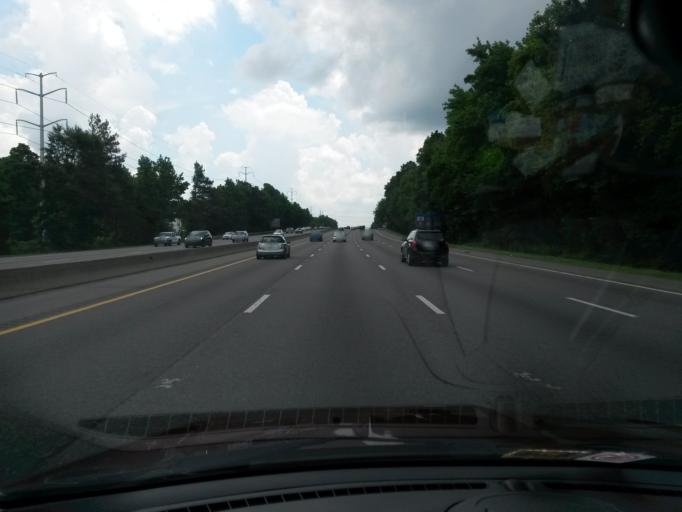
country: US
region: Virginia
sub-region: Chesterfield County
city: Bellwood
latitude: 37.4230
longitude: -77.4286
